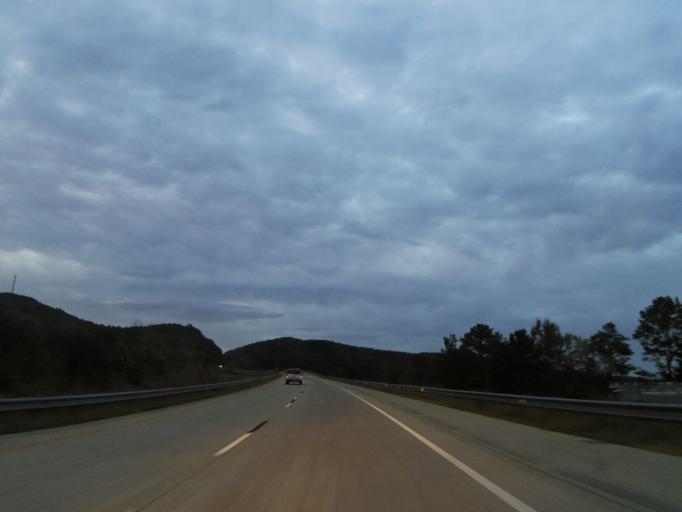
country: US
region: Alabama
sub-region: Etowah County
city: Whitesboro
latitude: 34.1232
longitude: -85.9811
